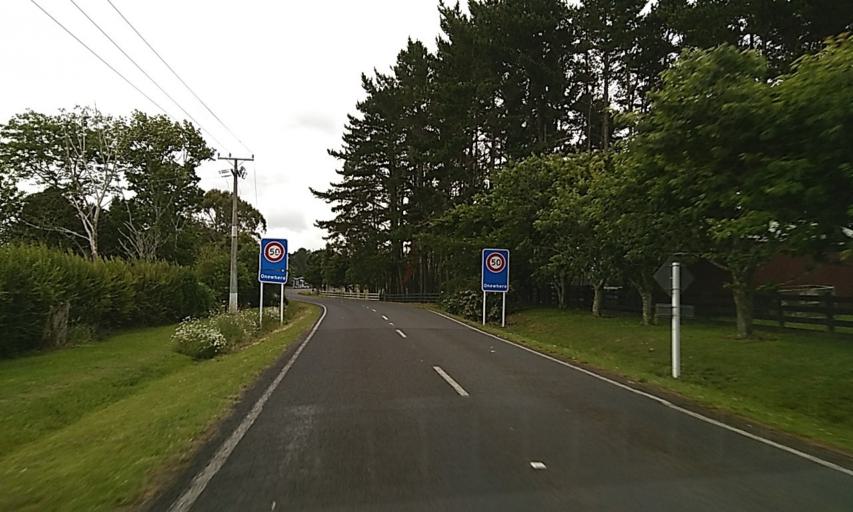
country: NZ
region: Auckland
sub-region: Auckland
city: Pukekohe East
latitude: -37.3235
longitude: 174.9182
